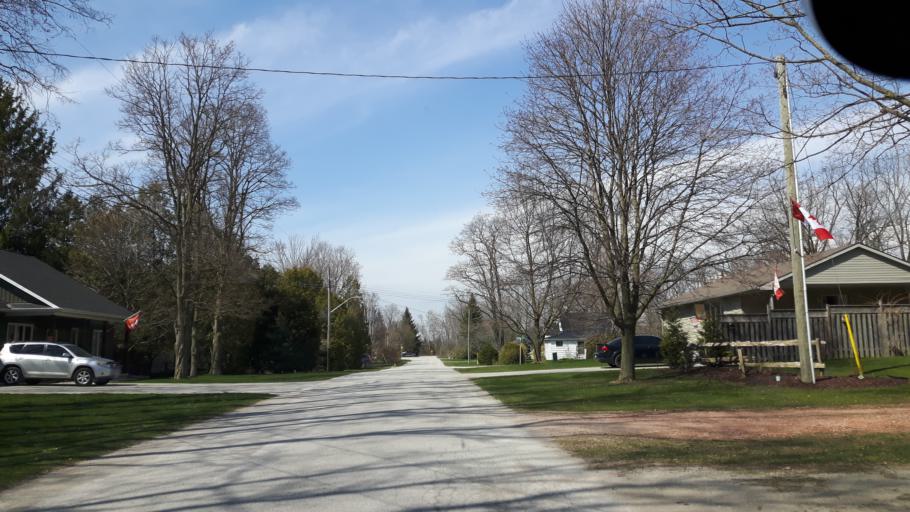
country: CA
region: Ontario
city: Bluewater
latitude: 43.5585
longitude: -81.6902
